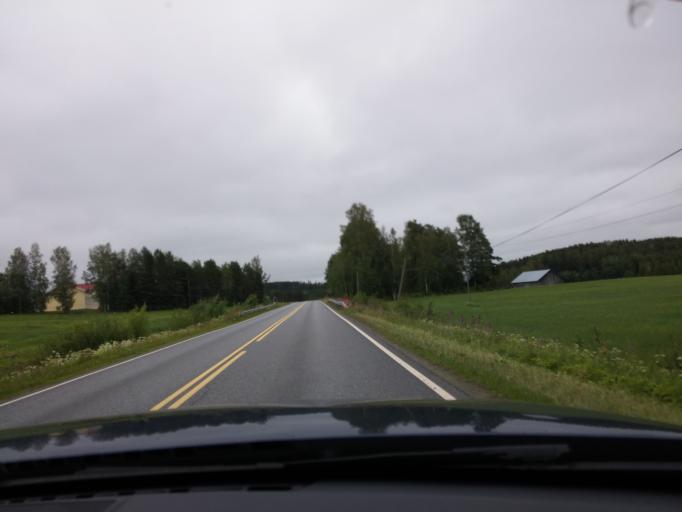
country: FI
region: Central Finland
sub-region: Joutsa
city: Joutsa
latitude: 61.8097
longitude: 25.9729
